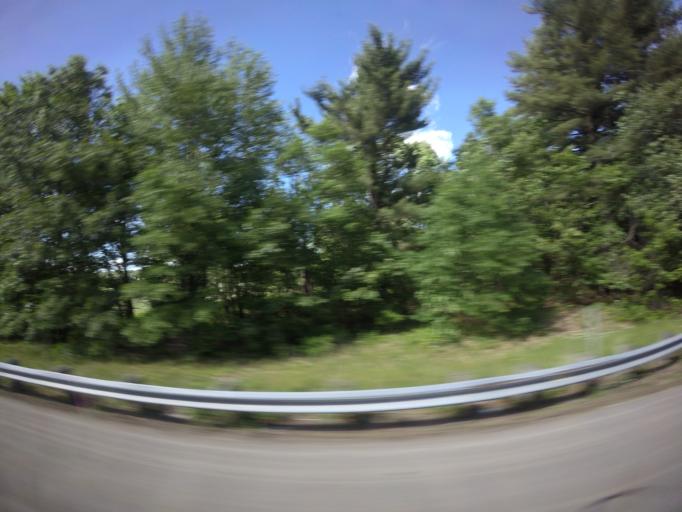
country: US
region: New Hampshire
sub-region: Hillsborough County
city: Manchester
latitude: 42.9607
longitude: -71.4115
